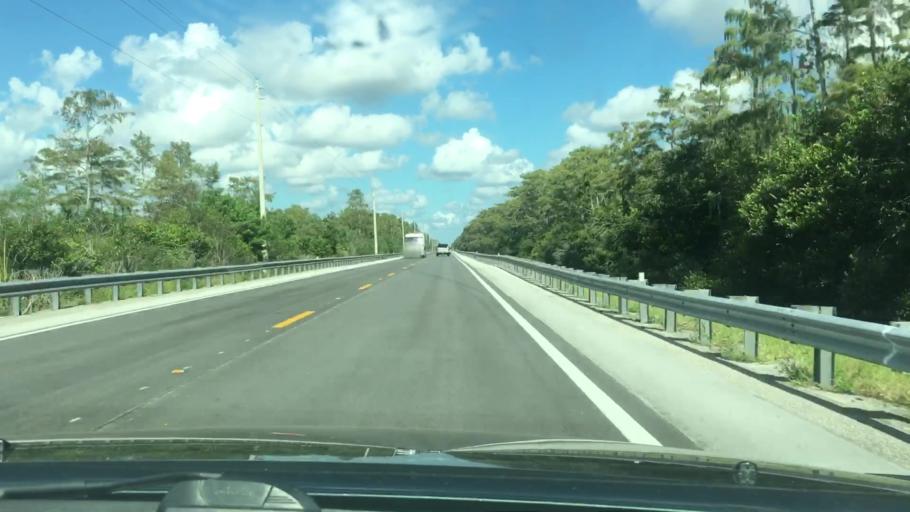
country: US
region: Florida
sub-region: Miami-Dade County
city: Kendall West
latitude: 25.7716
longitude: -80.8383
